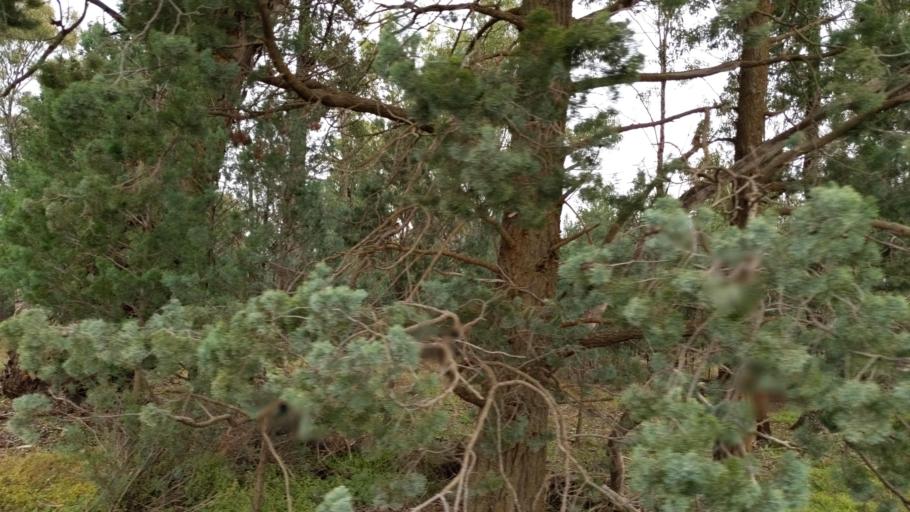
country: AU
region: New South Wales
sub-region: Coolamon
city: Coolamon
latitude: -34.8257
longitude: 146.9289
